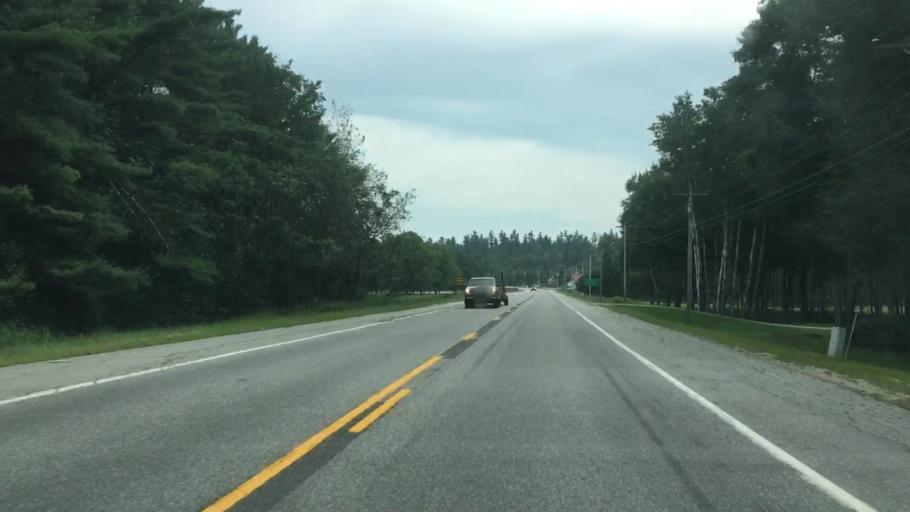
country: US
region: Maine
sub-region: Oxford County
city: Bethel
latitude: 44.4534
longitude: -70.8061
